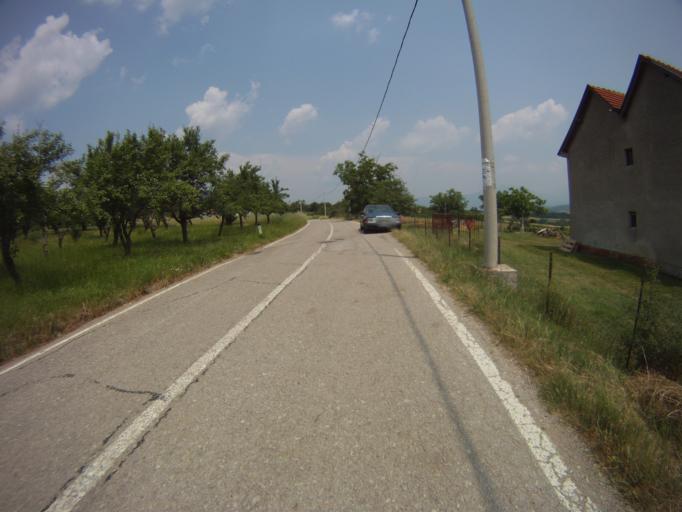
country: RS
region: Central Serbia
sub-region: Nisavski Okrug
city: Gadzin Han
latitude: 43.2016
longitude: 21.9591
